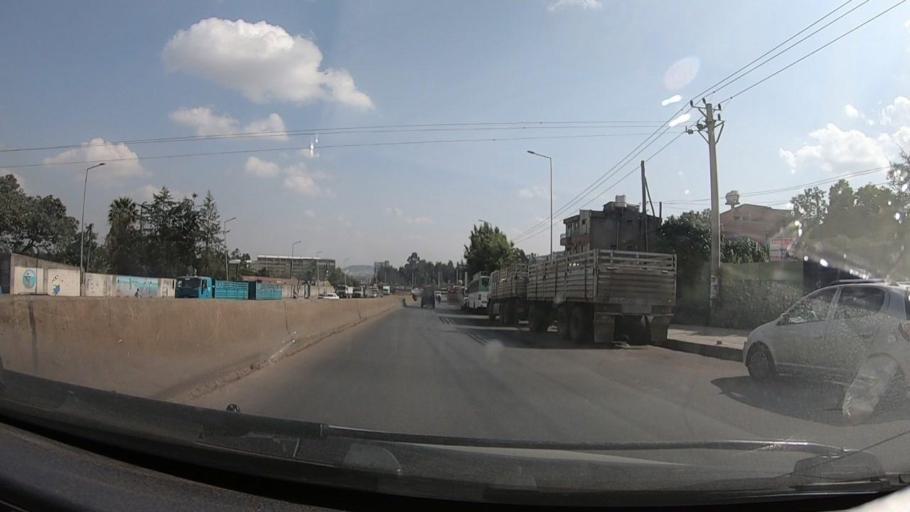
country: ET
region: Adis Abeba
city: Addis Ababa
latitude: 8.9868
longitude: 38.6936
